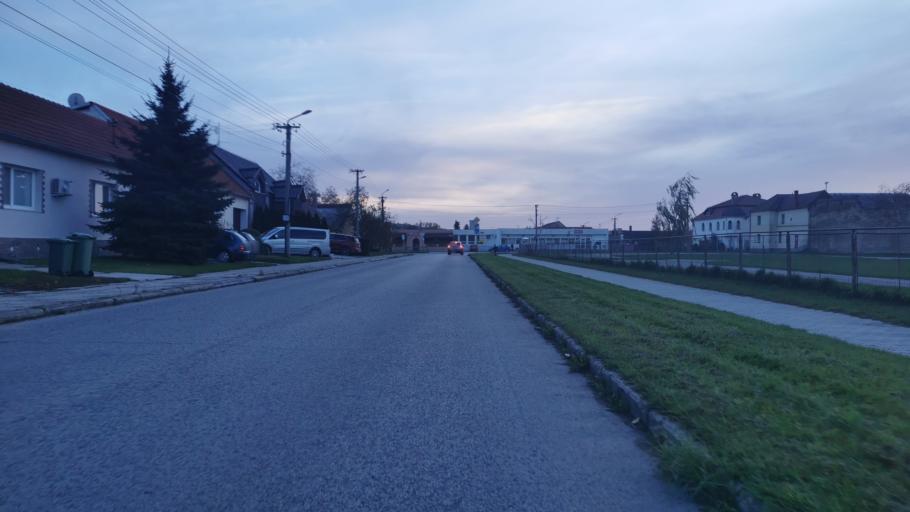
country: SK
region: Trnavsky
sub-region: Okres Skalica
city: Skalica
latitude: 48.8449
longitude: 17.2349
